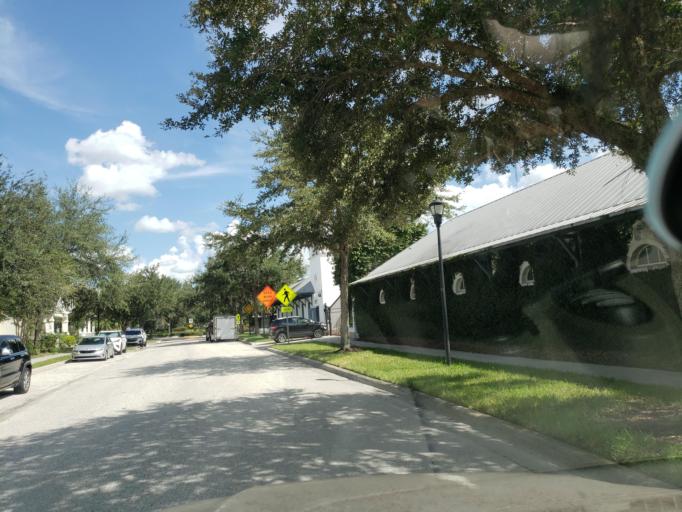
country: US
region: Florida
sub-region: Hillsborough County
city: Fish Hawk
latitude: 27.8405
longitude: -82.2172
